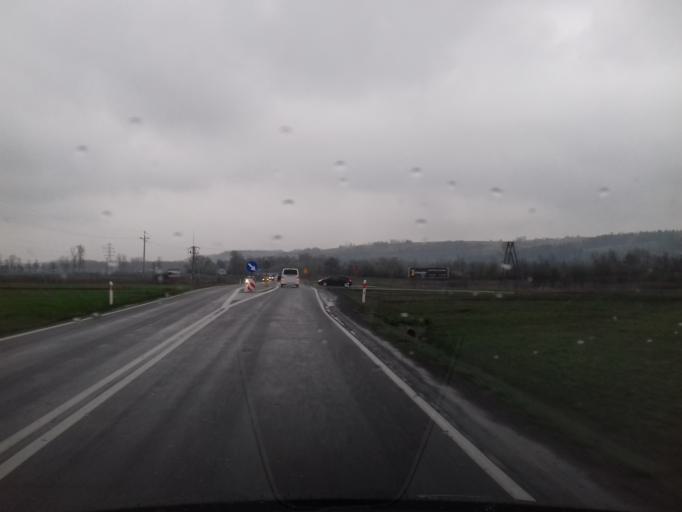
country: PL
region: Lesser Poland Voivodeship
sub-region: Powiat nowosadecki
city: Stary Sacz
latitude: 49.5467
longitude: 20.6510
